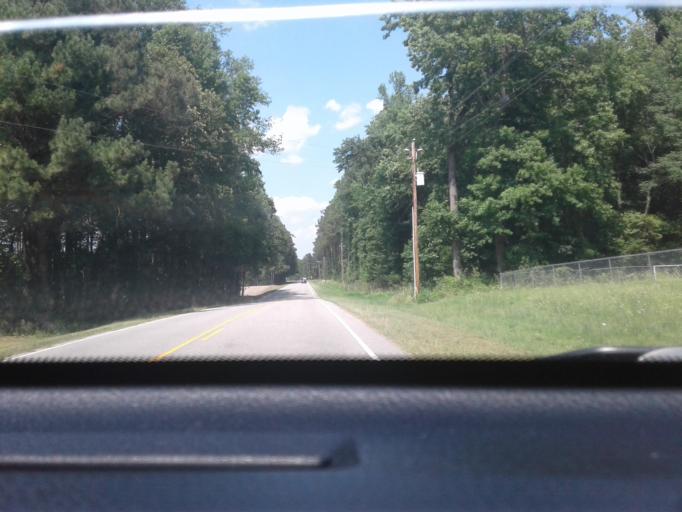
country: US
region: North Carolina
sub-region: Cumberland County
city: Eastover
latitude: 35.1820
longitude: -78.7070
